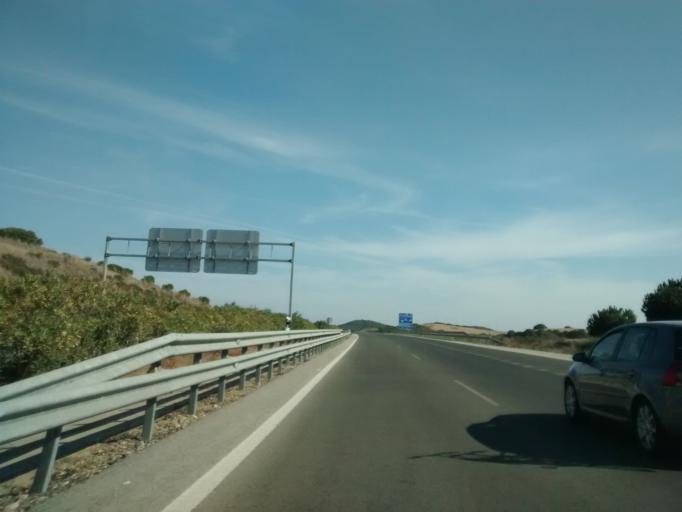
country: ES
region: Andalusia
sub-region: Provincia de Cadiz
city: Conil de la Frontera
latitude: 36.2990
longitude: -6.0565
